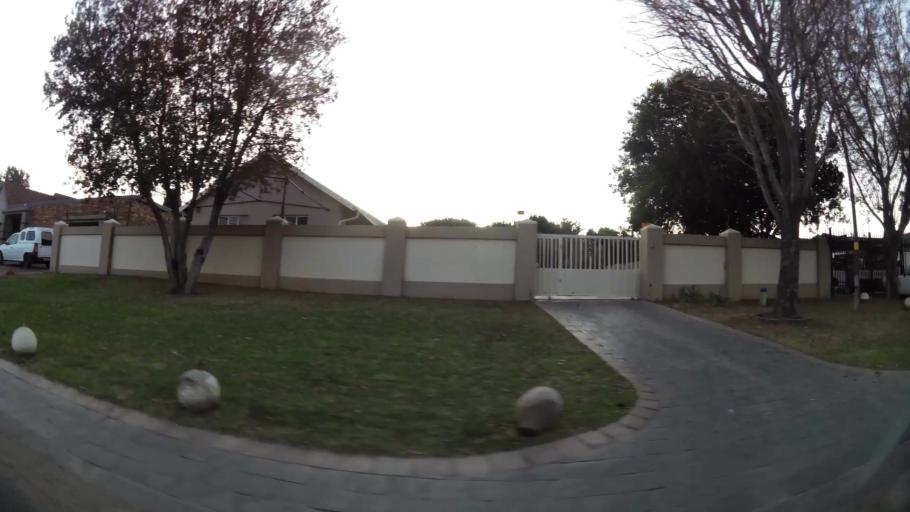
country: ZA
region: Gauteng
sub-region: City of Johannesburg Metropolitan Municipality
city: Modderfontein
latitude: -26.0768
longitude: 28.2235
